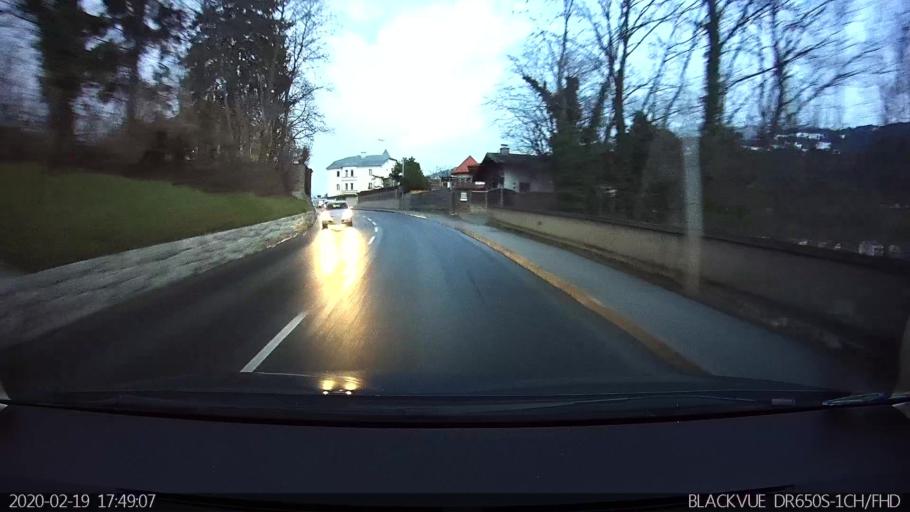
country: AT
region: Tyrol
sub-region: Politischer Bezirk Innsbruck Land
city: Hall in Tirol
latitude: 47.2803
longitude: 11.5181
